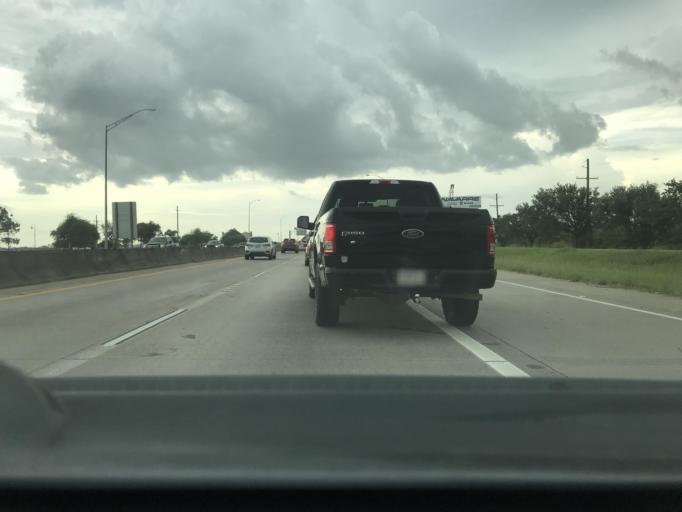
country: US
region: Louisiana
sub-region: Calcasieu Parish
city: Westlake
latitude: 30.2374
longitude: -93.2339
